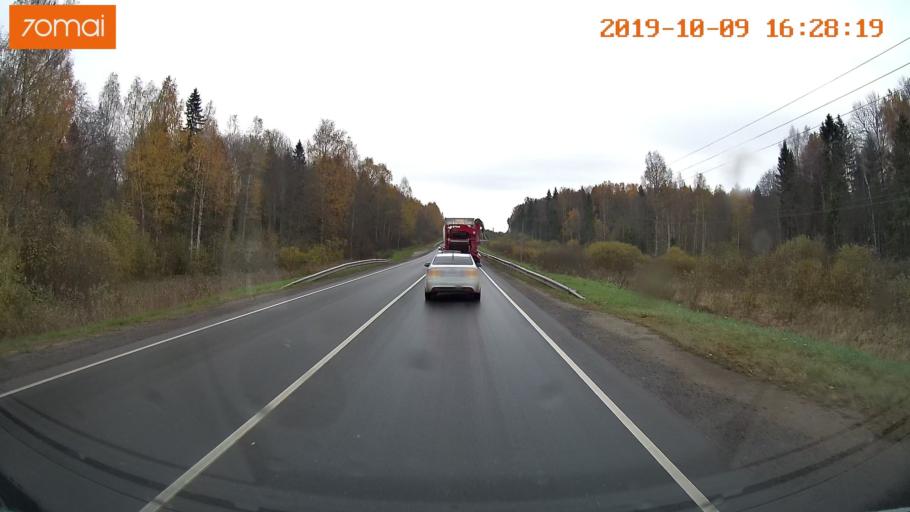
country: RU
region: Kostroma
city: Oktyabr'skiy
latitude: 57.6293
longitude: 40.9315
